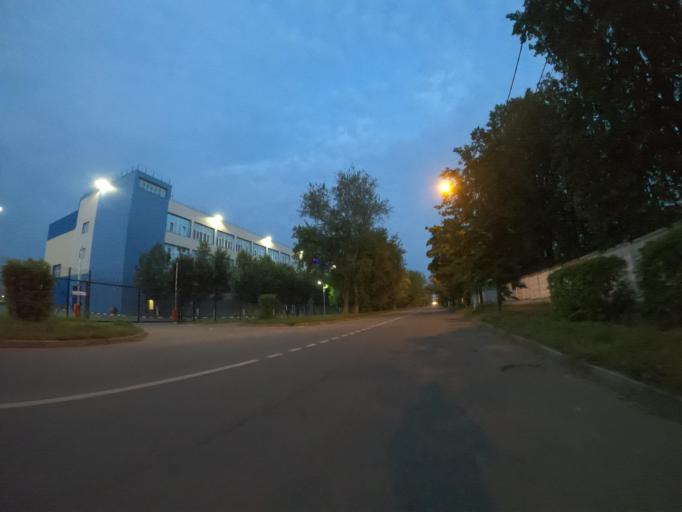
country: RU
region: Moskovskaya
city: Zhukovskiy
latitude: 55.6053
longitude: 38.1177
